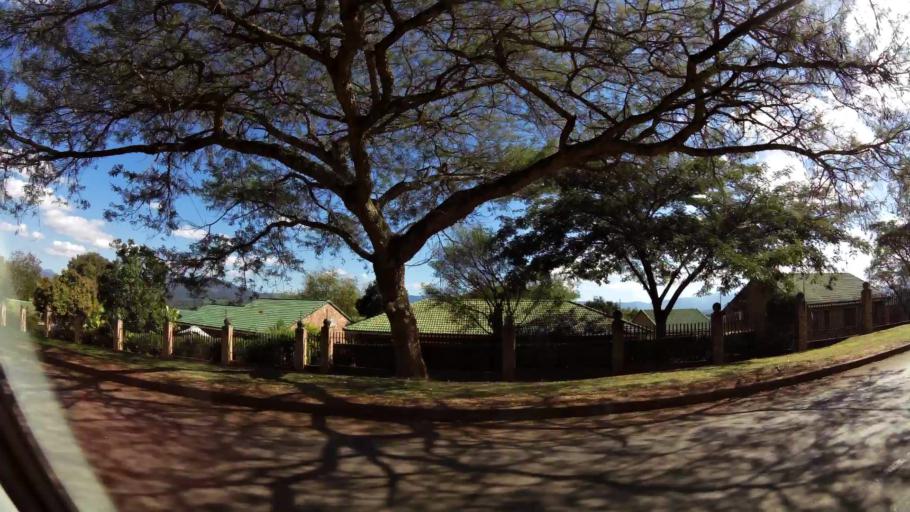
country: ZA
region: Limpopo
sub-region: Mopani District Municipality
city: Tzaneen
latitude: -23.8198
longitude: 30.1441
